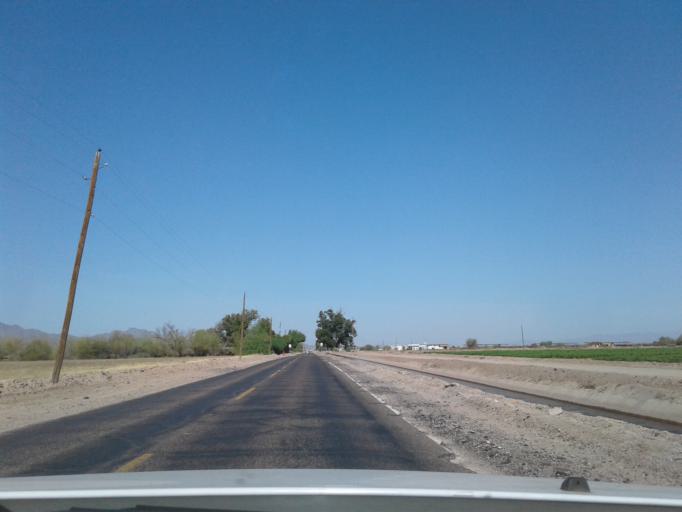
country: US
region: Arizona
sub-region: Maricopa County
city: Laveen
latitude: 33.3629
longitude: -112.1882
